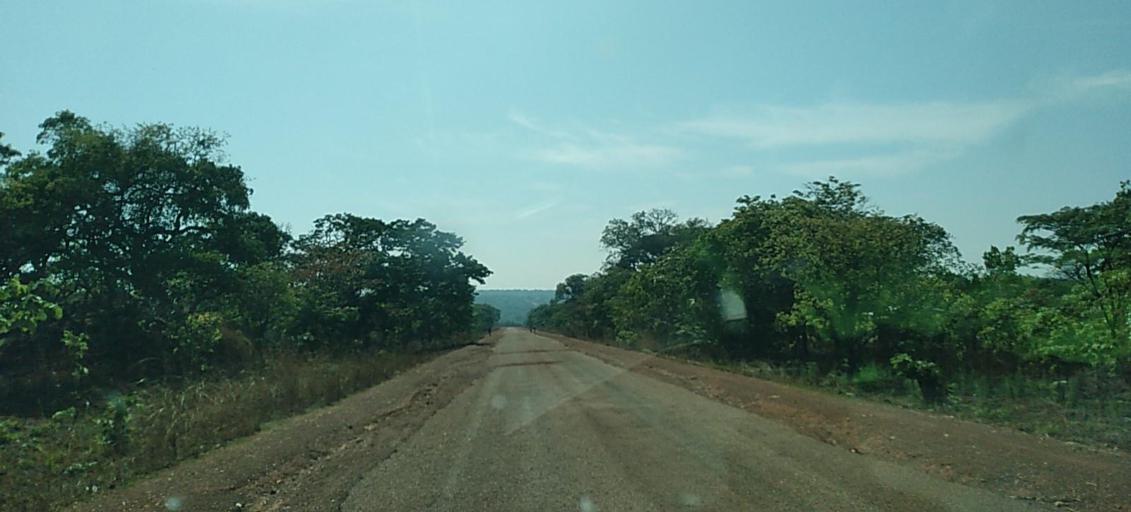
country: ZM
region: North-Western
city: Mwinilunga
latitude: -11.8228
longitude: 25.1136
